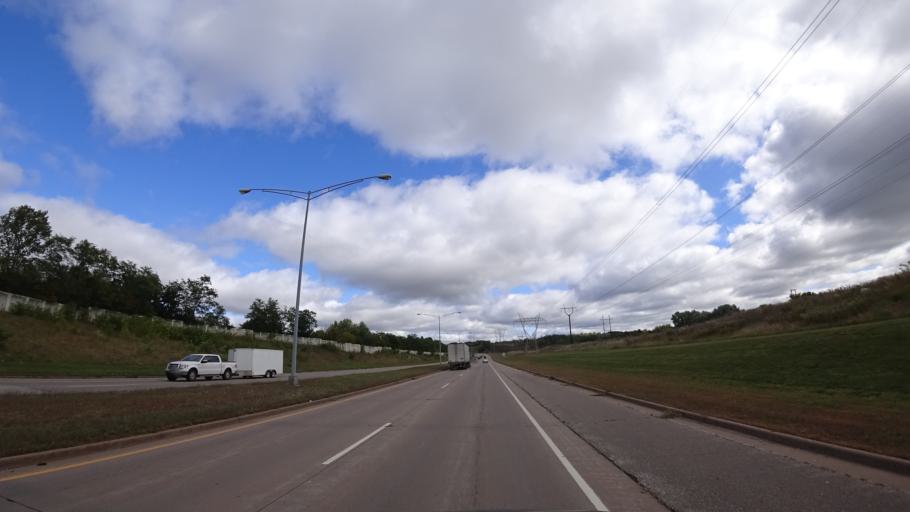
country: US
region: Wisconsin
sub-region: Eau Claire County
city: Eau Claire
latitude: 44.8408
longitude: -91.4938
